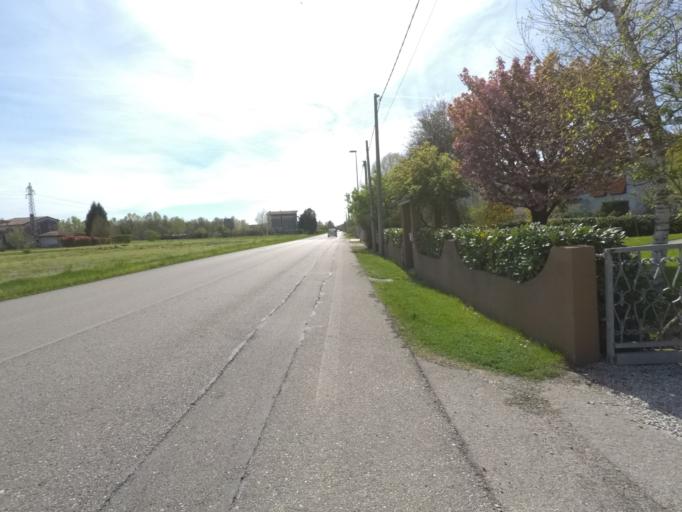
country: IT
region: Friuli Venezia Giulia
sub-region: Provincia di Pordenone
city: Fiume Veneto
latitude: 45.9364
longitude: 12.7425
